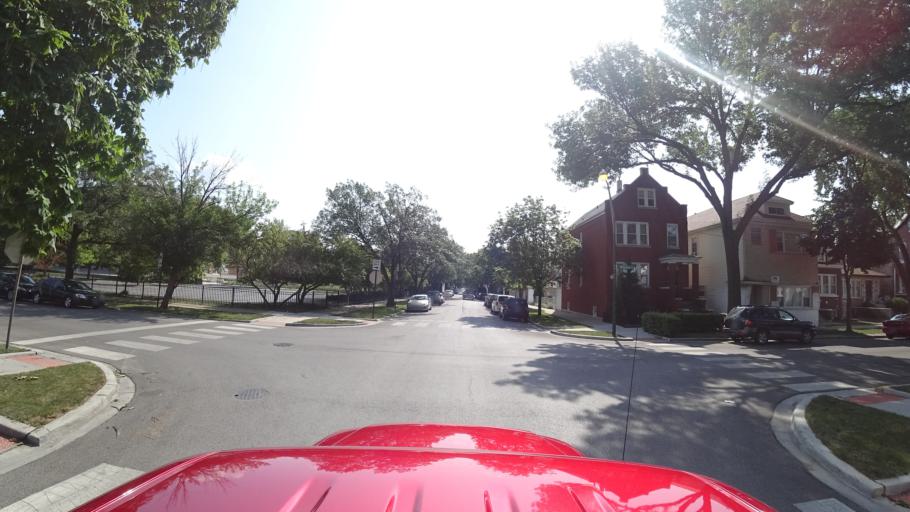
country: US
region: Illinois
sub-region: Cook County
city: Cicero
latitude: 41.8118
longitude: -87.7007
